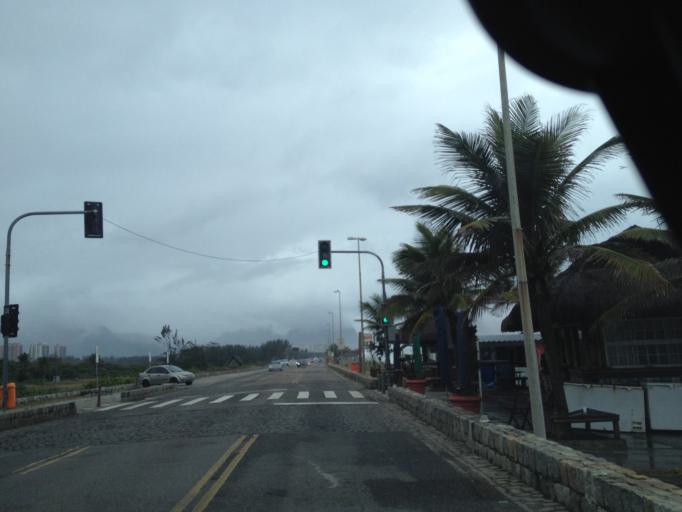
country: BR
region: Rio de Janeiro
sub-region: Nilopolis
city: Nilopolis
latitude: -23.0139
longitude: -43.3998
